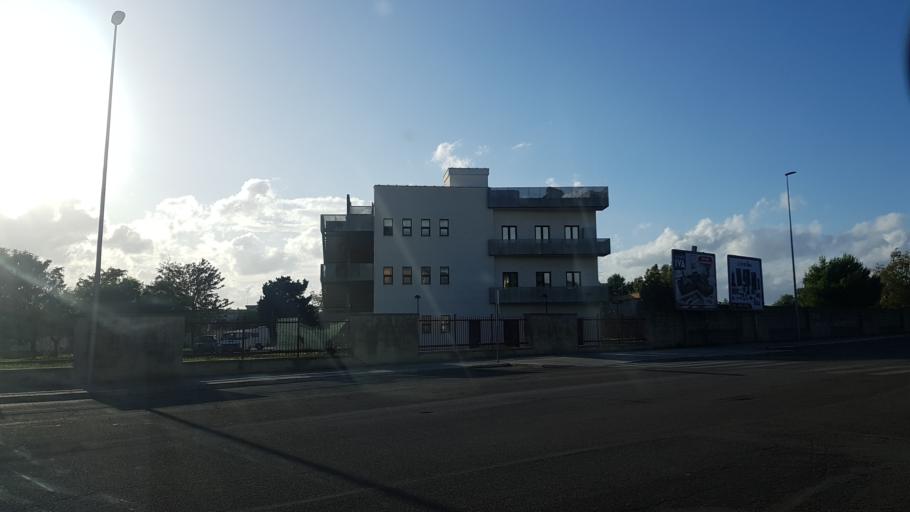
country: IT
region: Apulia
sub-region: Provincia di Lecce
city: Lecce
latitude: 40.3536
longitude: 18.1541
